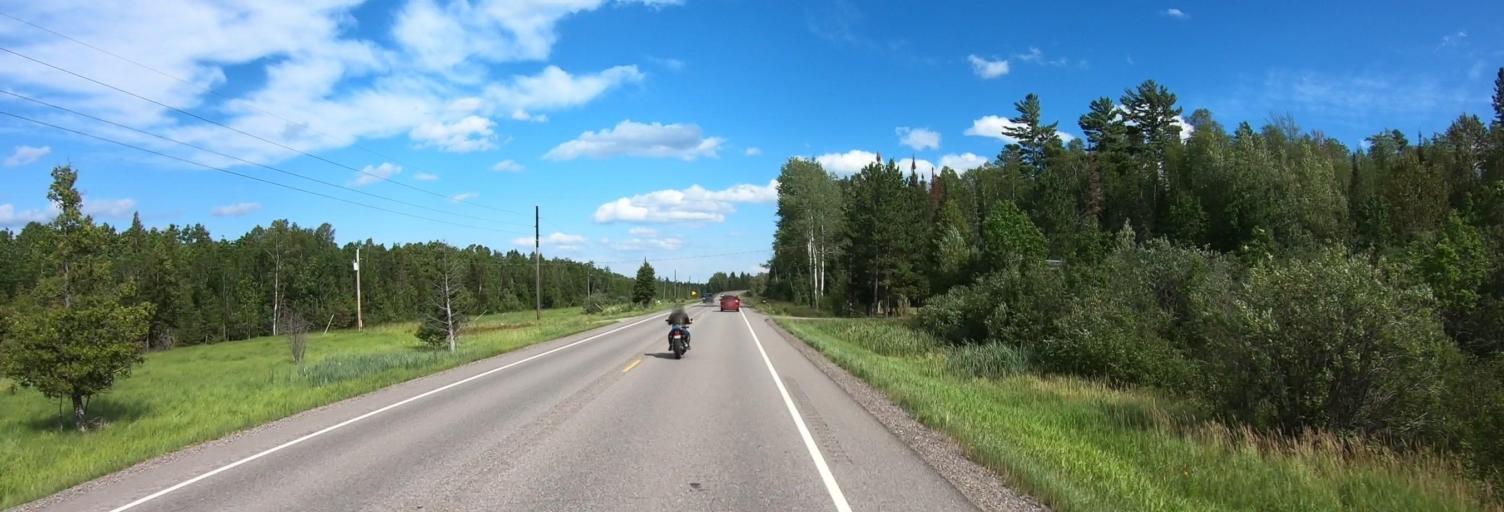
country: US
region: Minnesota
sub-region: Saint Louis County
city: Ely
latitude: 47.8836
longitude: -91.9912
